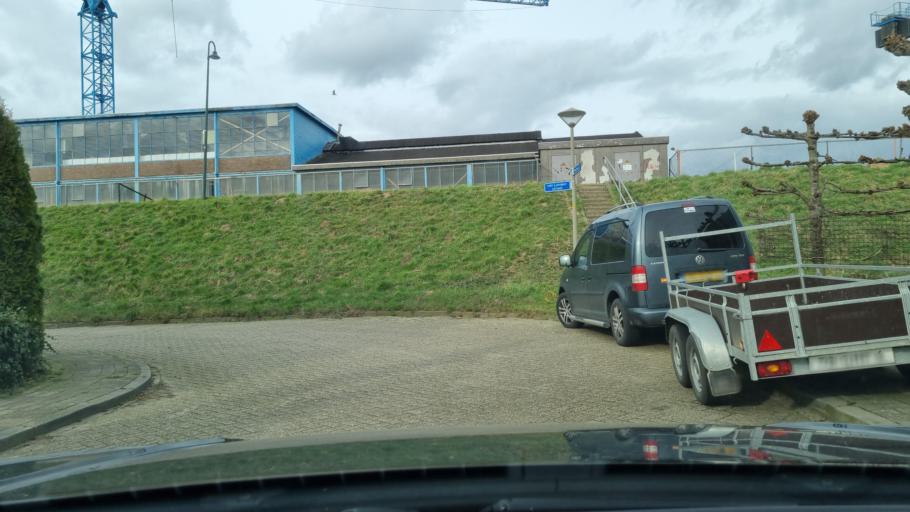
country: NL
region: Gelderland
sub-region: Gemeente Zevenaar
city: Zevenaar
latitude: 51.8669
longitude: 6.0510
